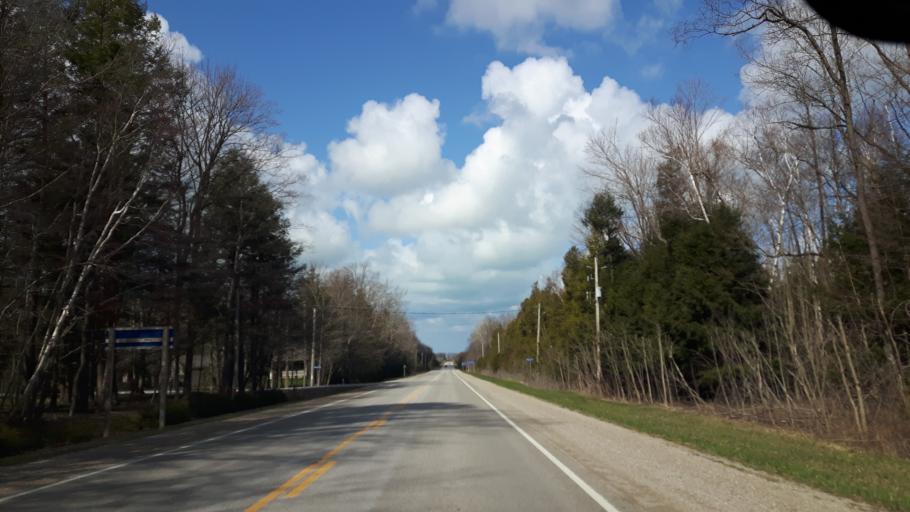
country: CA
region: Ontario
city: Bluewater
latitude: 43.5872
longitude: -81.6863
